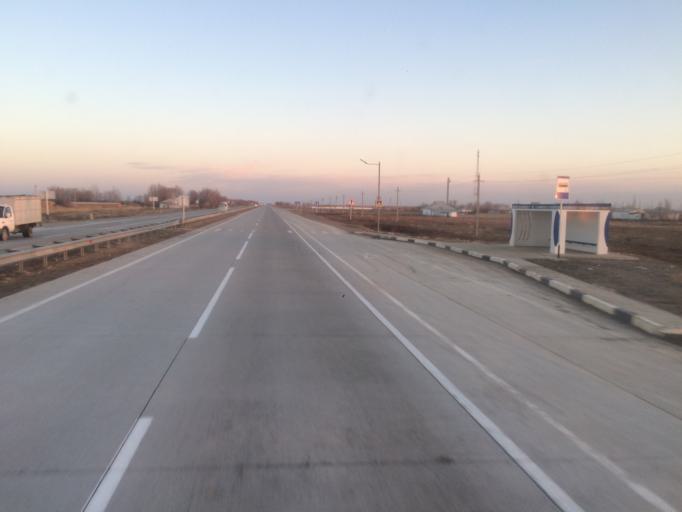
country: KZ
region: Ongtustik Qazaqstan
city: Bayaldyr
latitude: 43.0627
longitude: 68.6800
